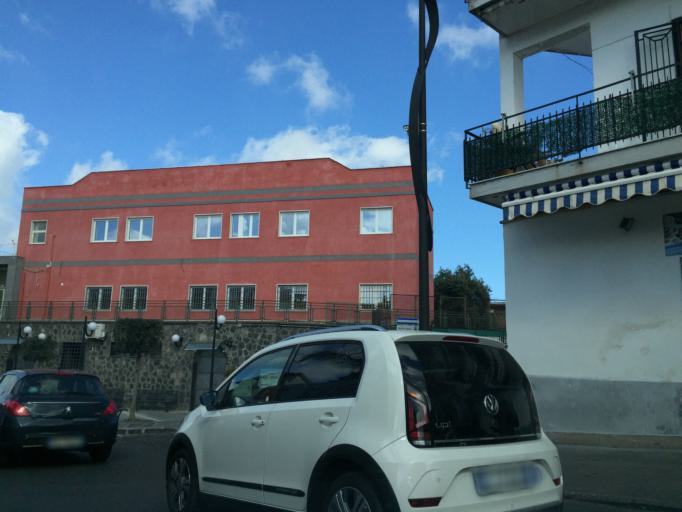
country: IT
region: Campania
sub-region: Provincia di Napoli
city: Massa di Somma
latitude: 40.8483
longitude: 14.3753
